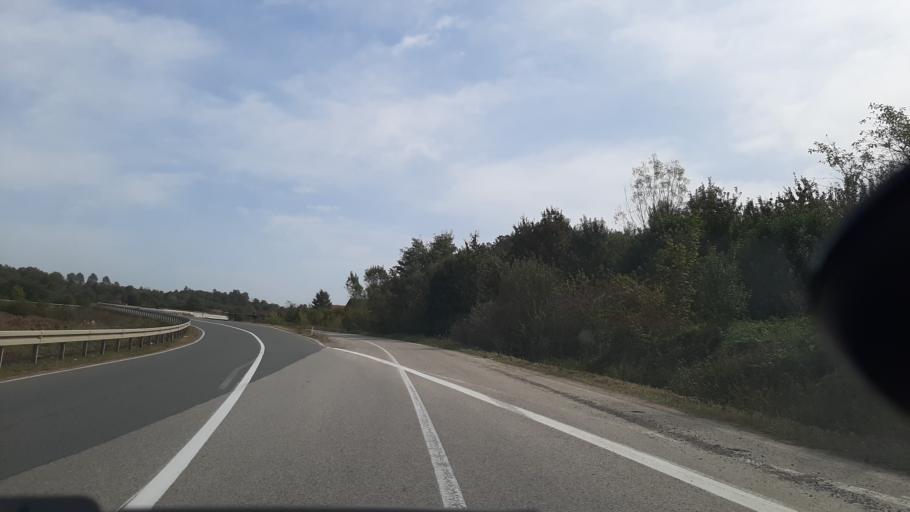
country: BA
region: Republika Srpska
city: Maglajani
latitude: 44.8733
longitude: 17.3871
